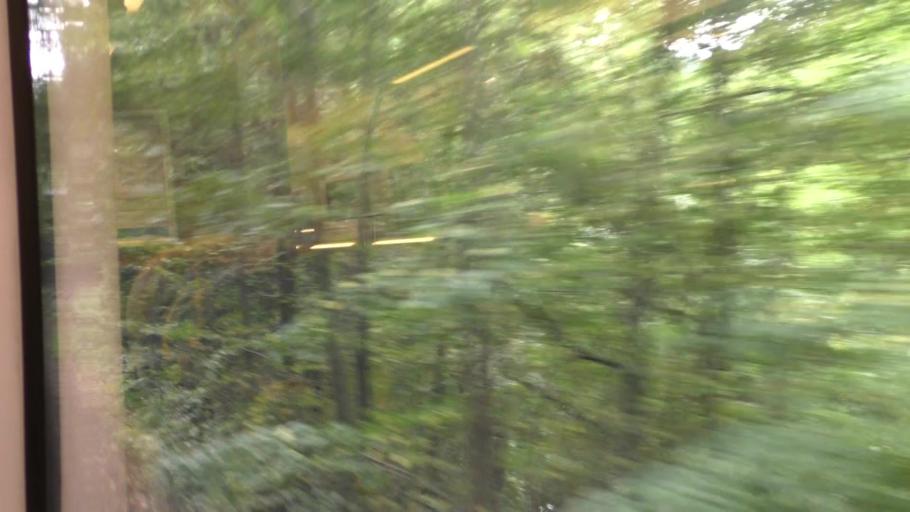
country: DE
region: Saxony
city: Hirschfelde
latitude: 50.9655
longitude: 14.9032
